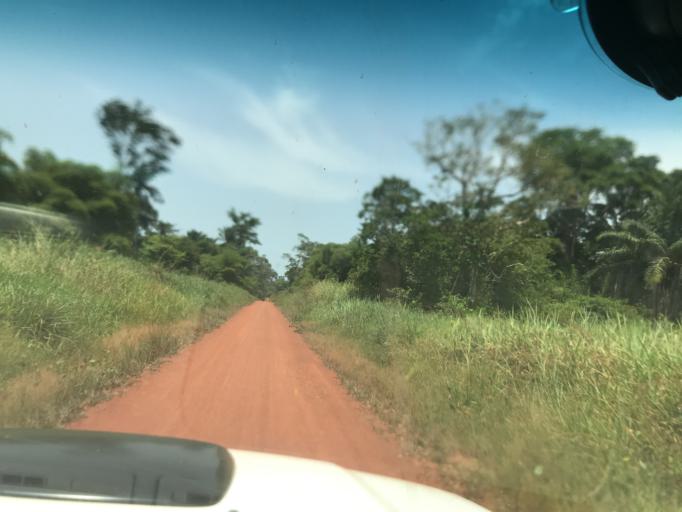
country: CD
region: Eastern Province
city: Aketi
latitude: 2.8743
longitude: 23.9544
